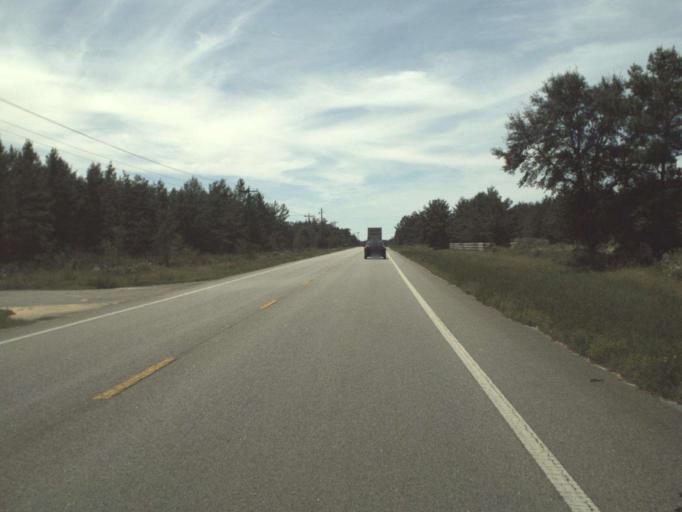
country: US
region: Florida
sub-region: Bay County
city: Lynn Haven
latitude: 30.4570
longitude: -85.6814
